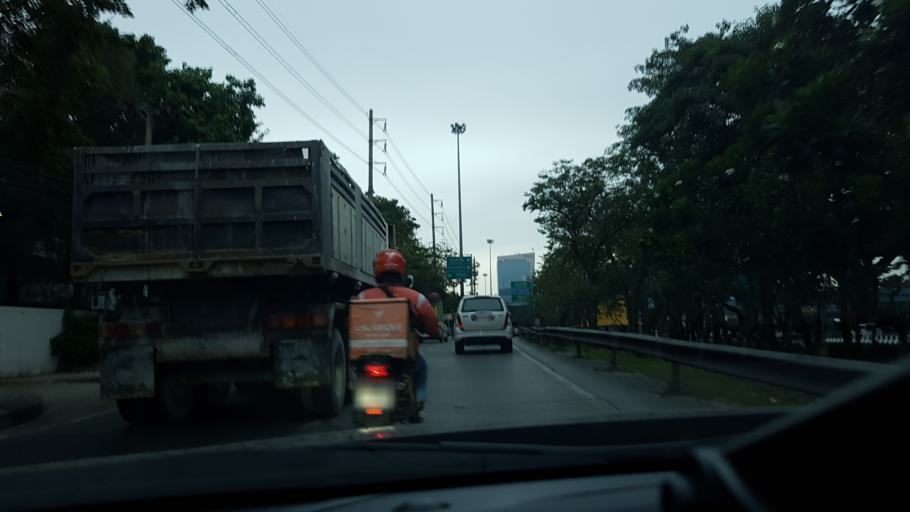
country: TH
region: Bangkok
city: Chatuchak
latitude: 13.8349
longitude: 100.5577
